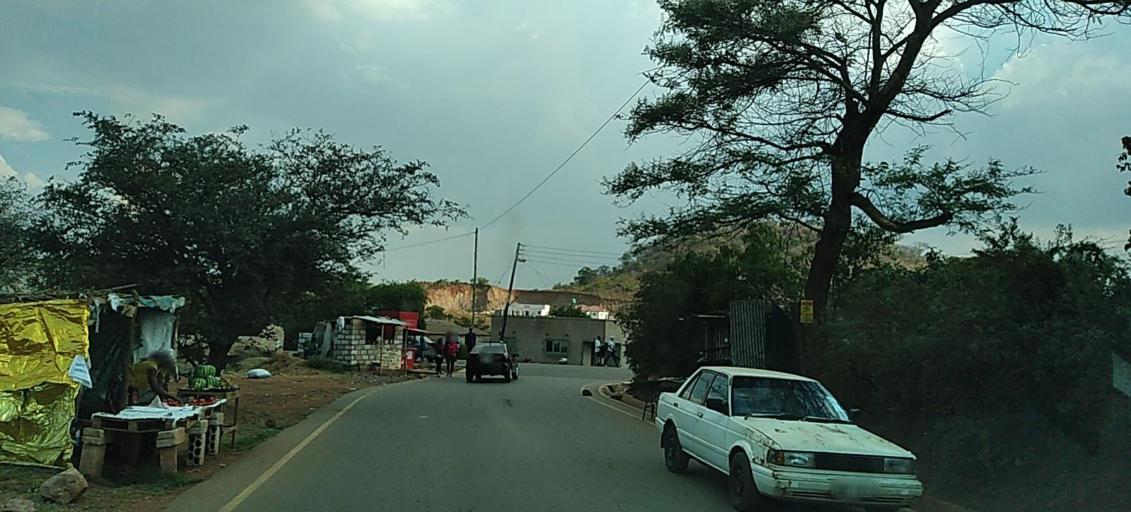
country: ZM
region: Lusaka
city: Lusaka
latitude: -15.5400
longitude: 28.2388
